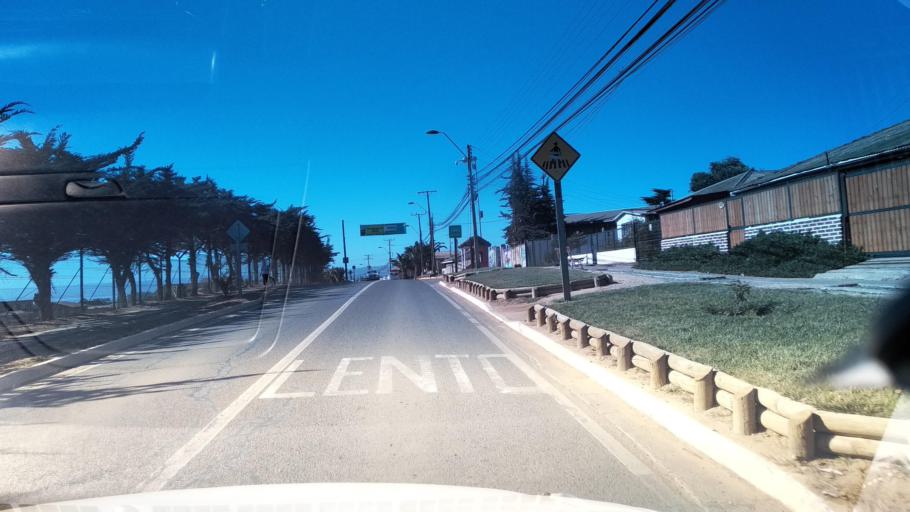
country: CL
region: O'Higgins
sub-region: Provincia de Colchagua
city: Santa Cruz
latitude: -34.3944
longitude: -72.0172
